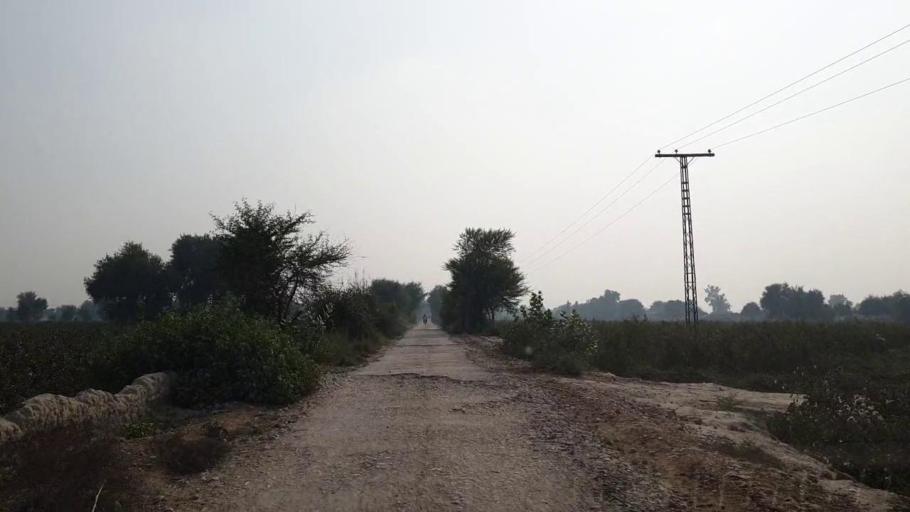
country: PK
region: Sindh
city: Bhan
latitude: 26.5853
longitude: 67.7307
